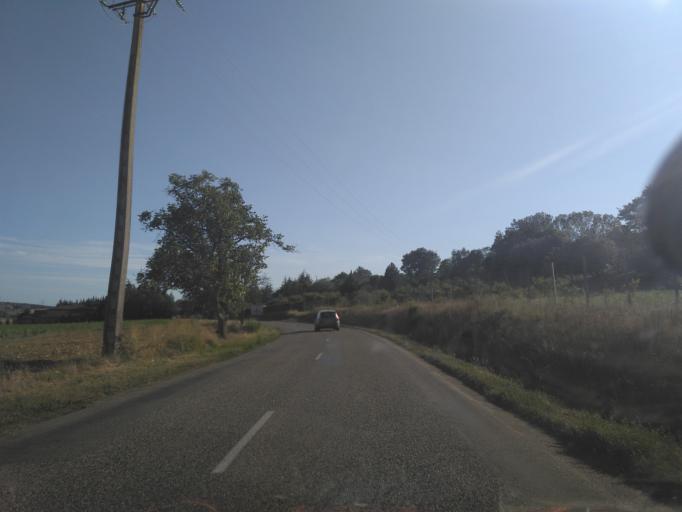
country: FR
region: Rhone-Alpes
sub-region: Departement de la Drome
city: Clerieux
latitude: 45.1062
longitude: 4.9505
